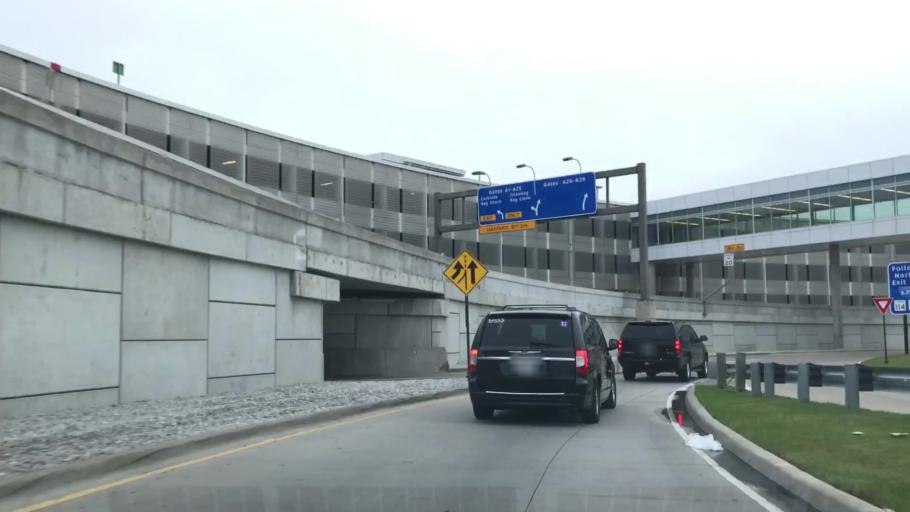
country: US
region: Texas
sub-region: Tarrant County
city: Grapevine
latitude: 32.9053
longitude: -97.0380
